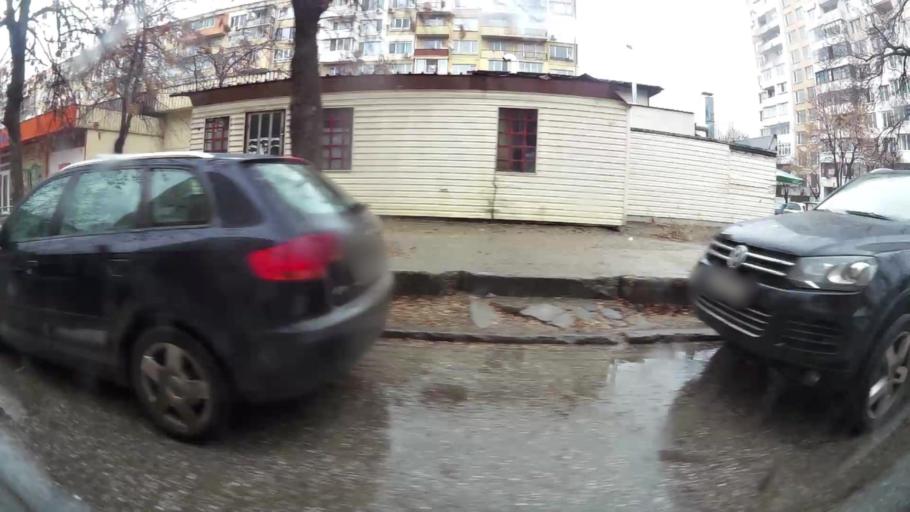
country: BG
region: Sofia-Capital
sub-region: Stolichna Obshtina
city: Sofia
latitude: 42.6695
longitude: 23.3968
